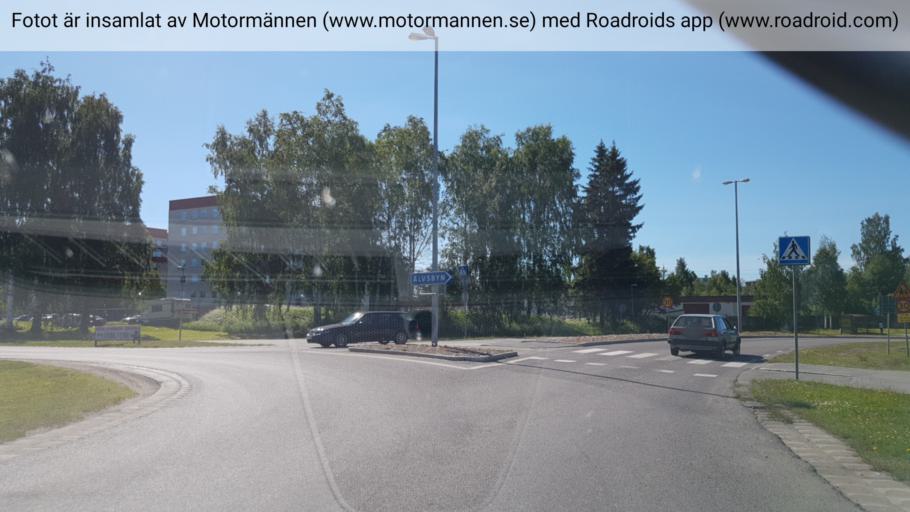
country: SE
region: Norrbotten
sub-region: Bodens Kommun
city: Boden
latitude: 65.8234
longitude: 21.6681
